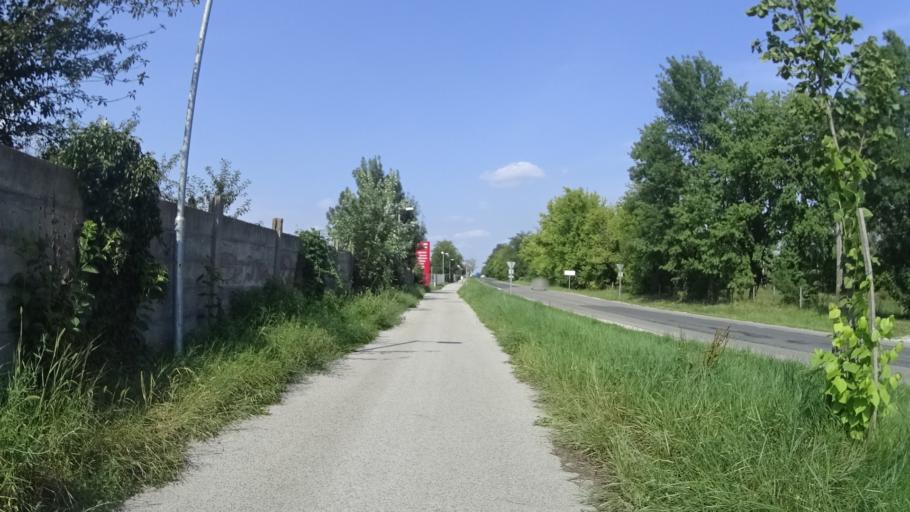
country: HU
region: Zala
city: Nagykanizsa
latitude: 46.4672
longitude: 17.0025
